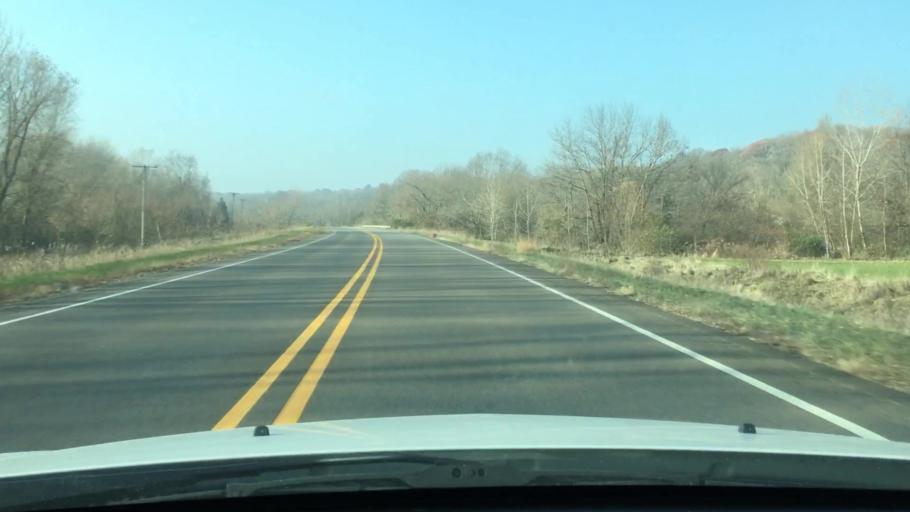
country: US
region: Illinois
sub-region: Peoria County
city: Glasford
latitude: 40.5496
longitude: -89.8519
